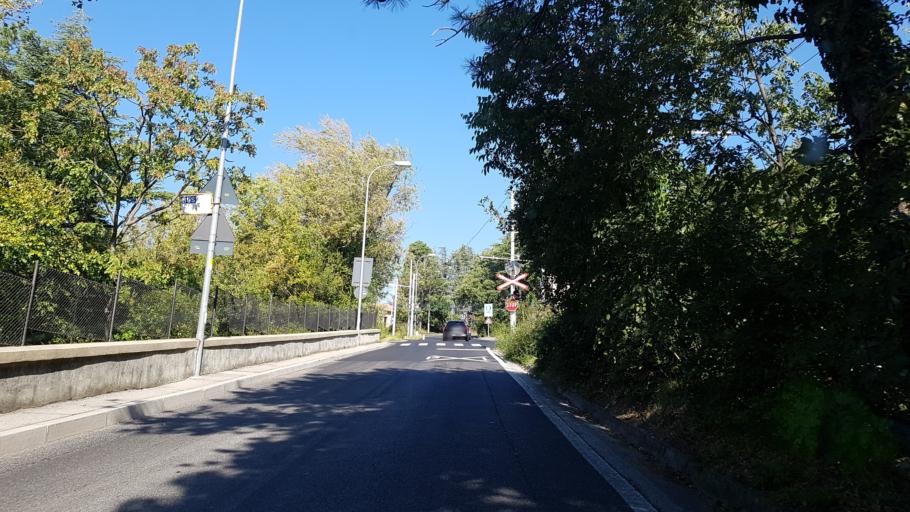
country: IT
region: Friuli Venezia Giulia
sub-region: Provincia di Trieste
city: Villa Opicina
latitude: 45.6659
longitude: 13.7865
